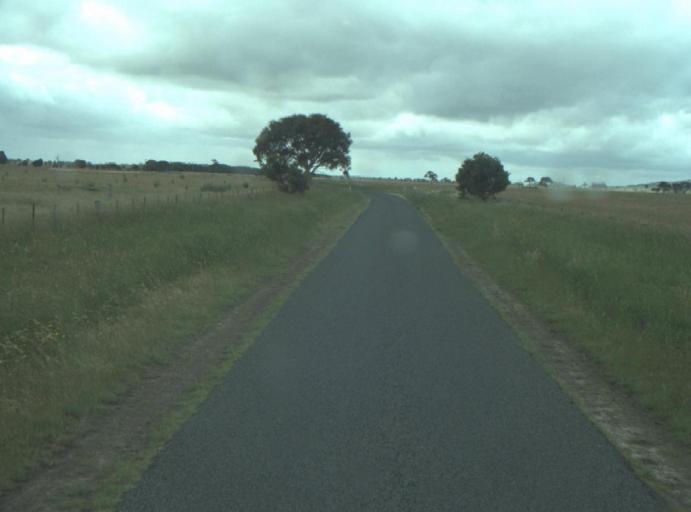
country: AU
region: Victoria
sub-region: Greater Geelong
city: Lara
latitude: -37.8488
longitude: 144.3543
